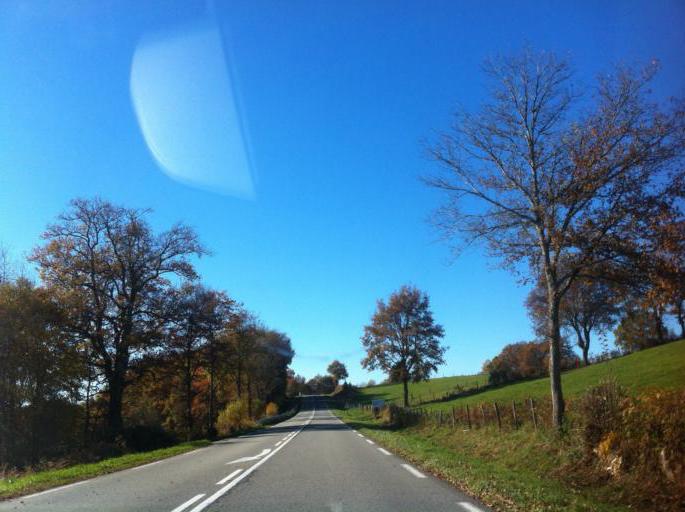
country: FR
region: Limousin
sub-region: Departement de la Creuse
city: Auzances
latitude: 45.8592
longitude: 2.5851
